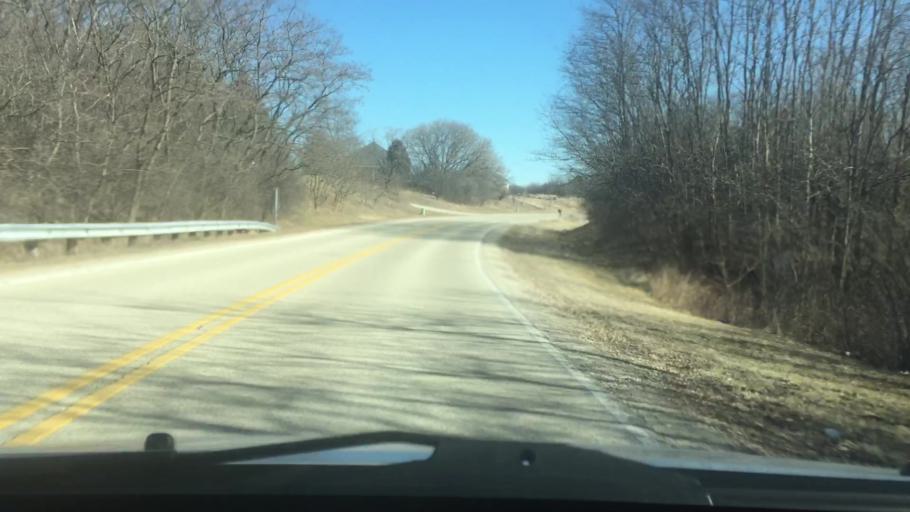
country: US
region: Wisconsin
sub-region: Waukesha County
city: Hartland
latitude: 43.1049
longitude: -88.3184
